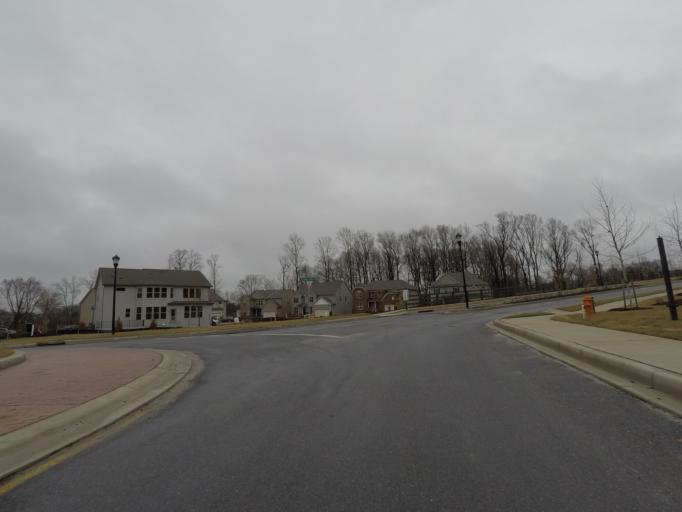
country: US
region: Maryland
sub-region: Howard County
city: Ellicott City
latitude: 39.3039
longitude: -76.8209
